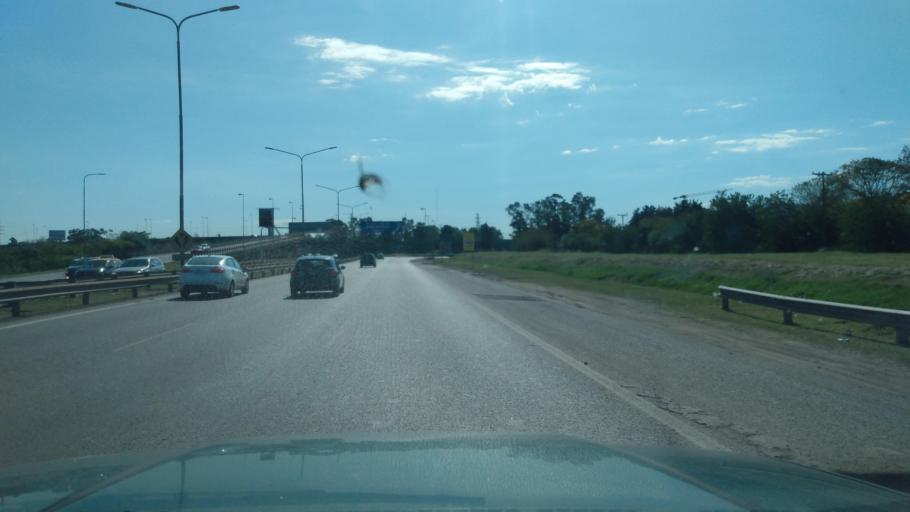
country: AR
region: Buenos Aires
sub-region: Partido de Tigre
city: Tigre
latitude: -34.4911
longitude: -58.5959
